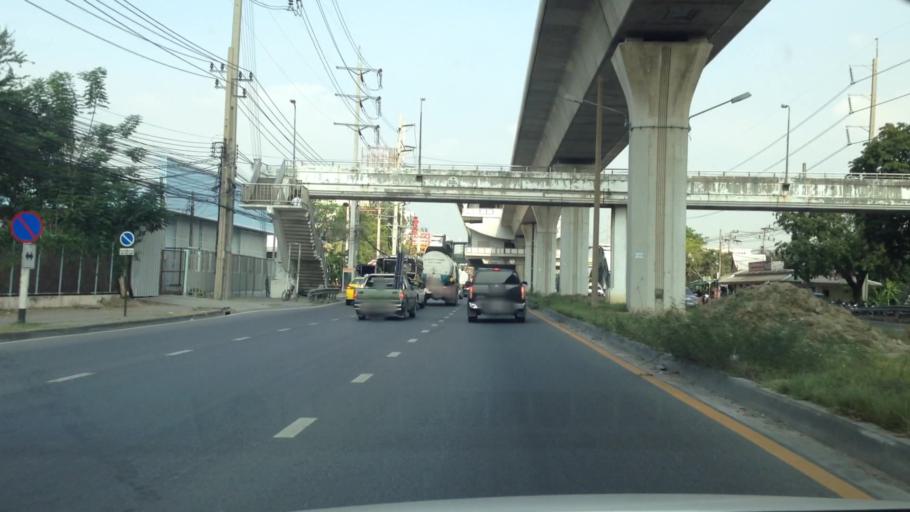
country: TH
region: Samut Prakan
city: Samut Prakan
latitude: 13.5656
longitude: 100.6086
